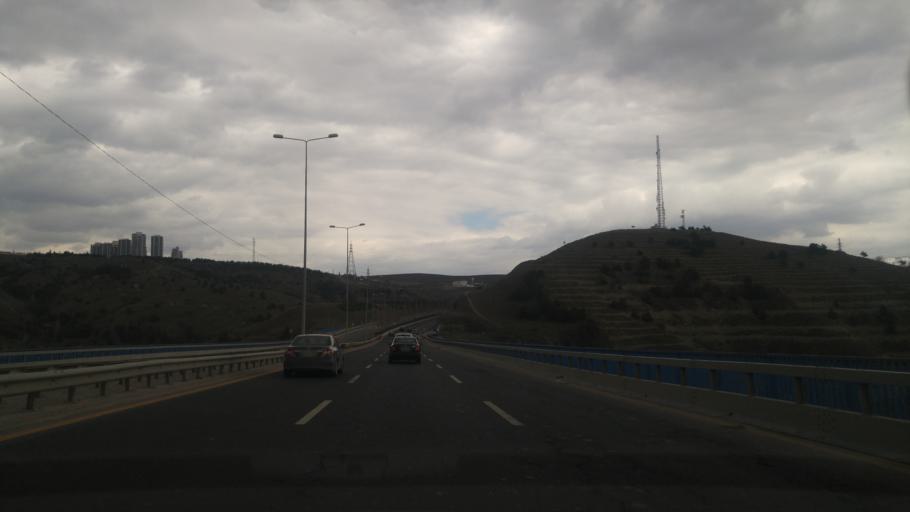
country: TR
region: Ankara
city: Mamak
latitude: 39.8888
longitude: 32.9088
